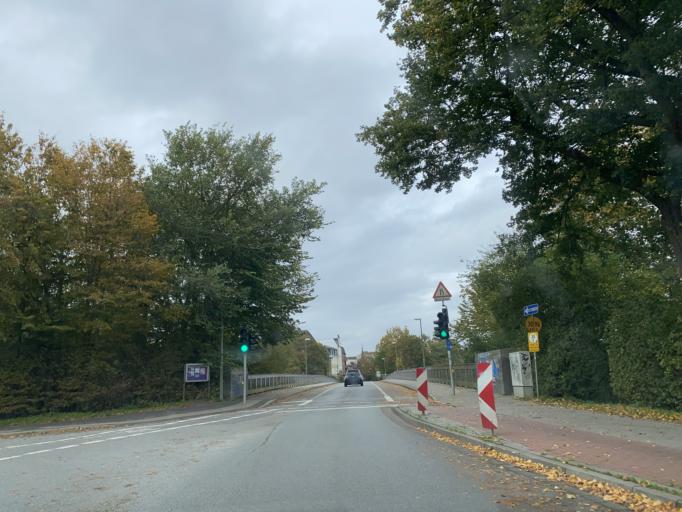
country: DE
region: Schleswig-Holstein
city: Flensburg
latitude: 54.7737
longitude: 9.4353
